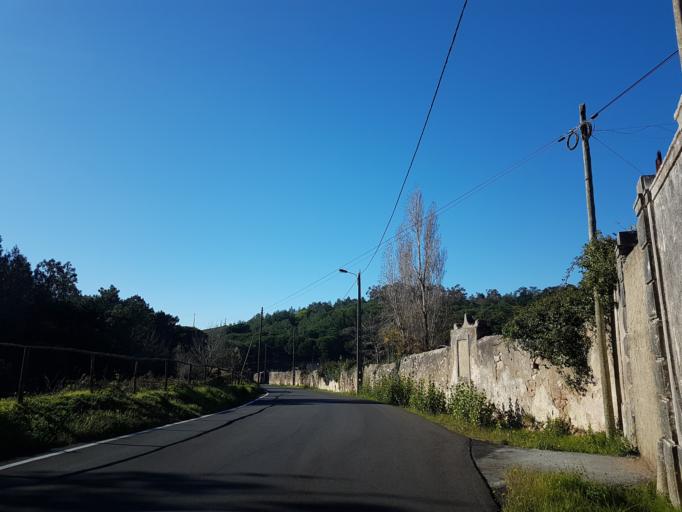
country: PT
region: Lisbon
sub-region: Cascais
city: Alcabideche
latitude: 38.7527
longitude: -9.4304
